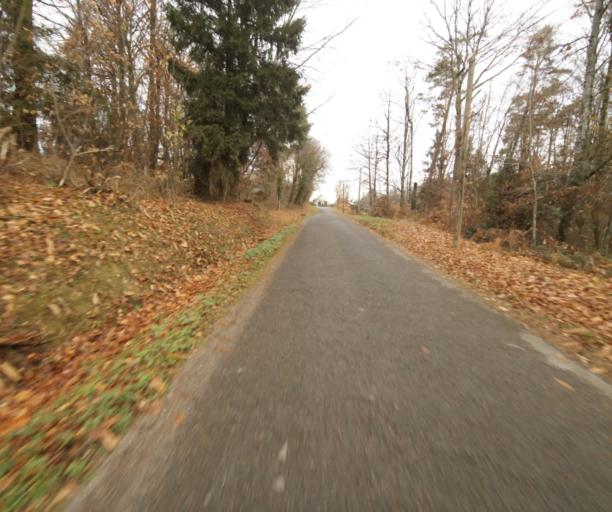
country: FR
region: Limousin
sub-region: Departement de la Correze
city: Tulle
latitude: 45.2649
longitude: 1.7336
